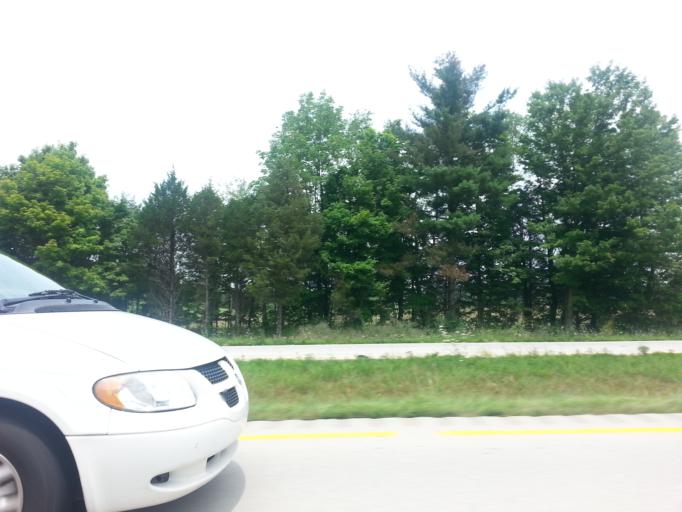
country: US
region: Kentucky
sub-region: Hardin County
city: Elizabethtown
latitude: 37.5623
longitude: -86.0634
